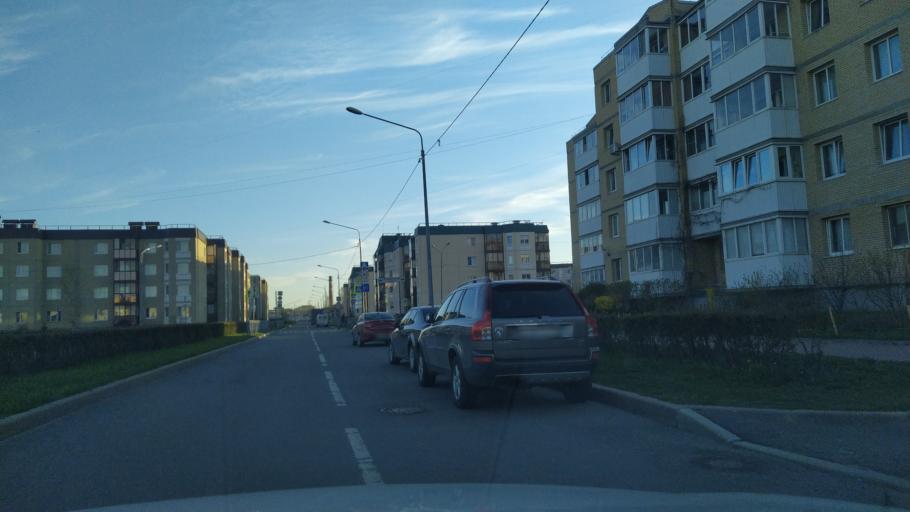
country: RU
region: St.-Petersburg
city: Pushkin
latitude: 59.7055
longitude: 30.3808
